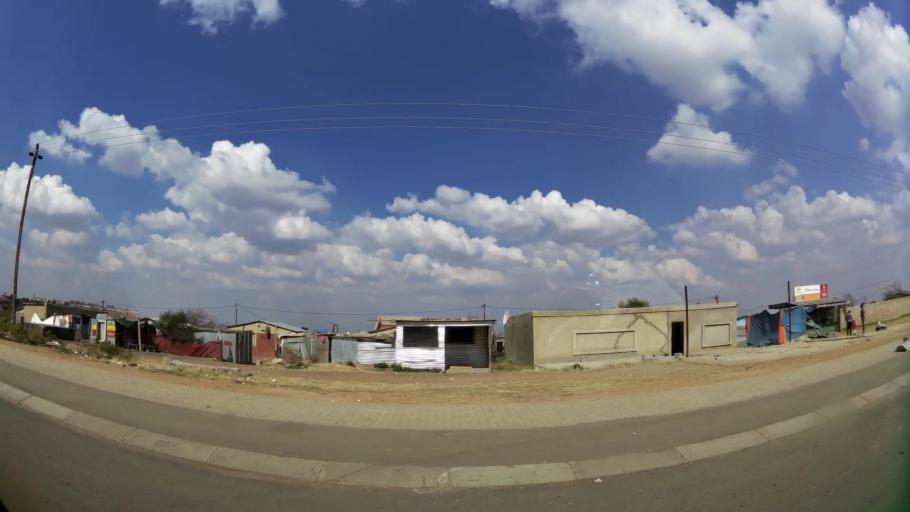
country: ZA
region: Gauteng
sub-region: City of Johannesburg Metropolitan Municipality
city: Roodepoort
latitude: -26.1936
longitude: 27.8735
